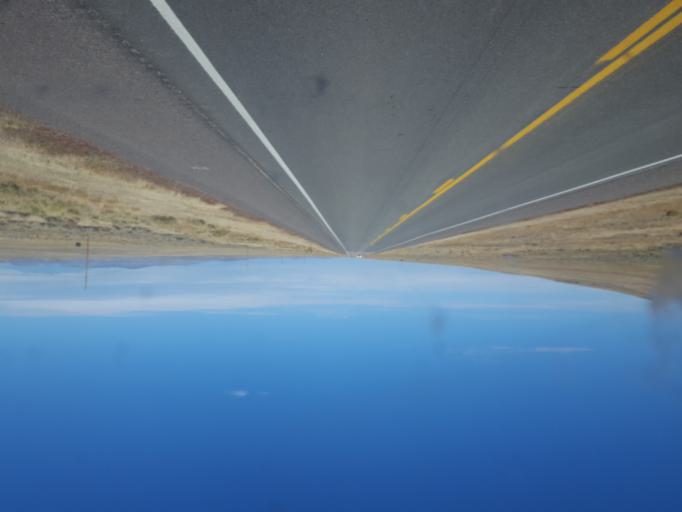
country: US
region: Colorado
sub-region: Conejos County
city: Conejos
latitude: 36.8371
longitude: -105.9731
